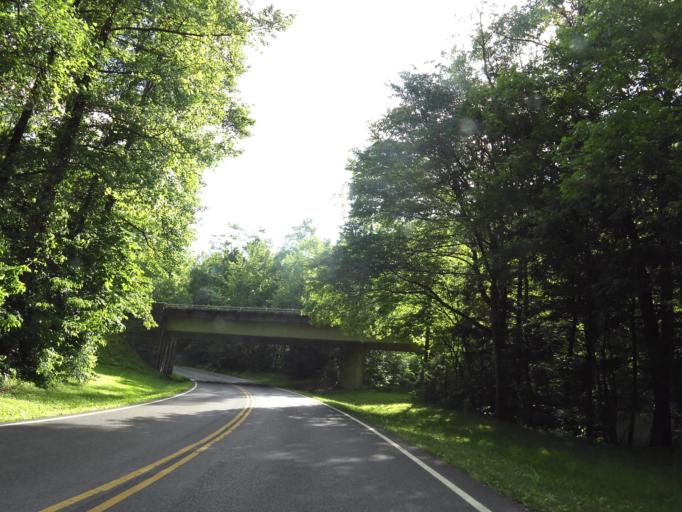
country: US
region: Tennessee
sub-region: Sevier County
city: Gatlinburg
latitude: 35.6950
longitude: -83.5299
